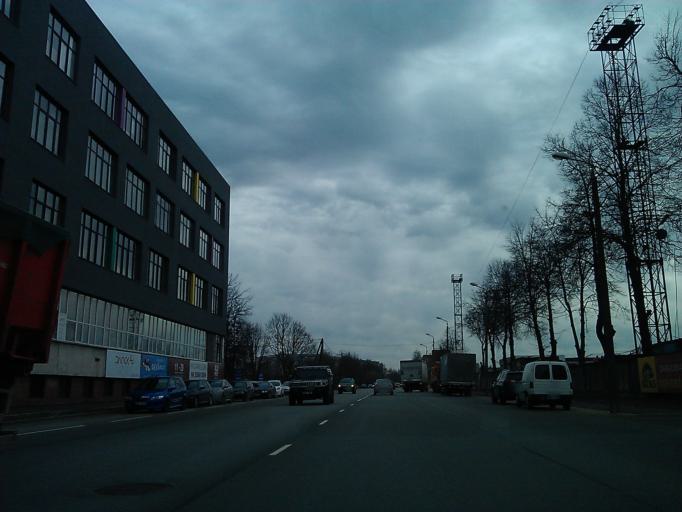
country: LV
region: Riga
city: Riga
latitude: 56.9615
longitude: 24.1651
